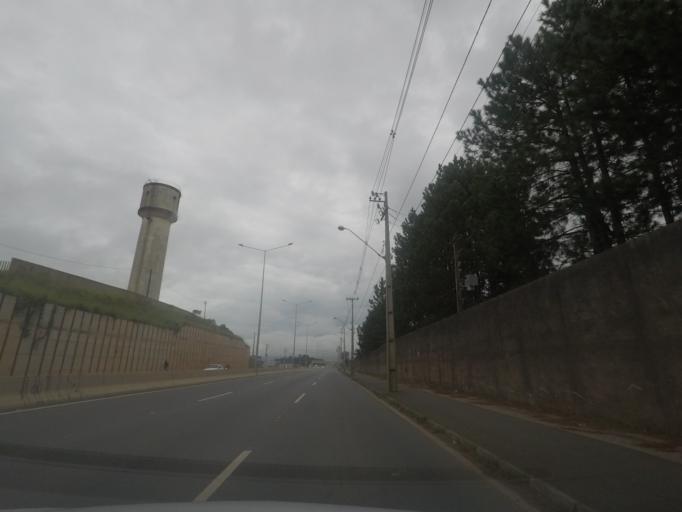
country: BR
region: Parana
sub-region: Piraquara
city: Piraquara
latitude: -25.4501
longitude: -49.1252
